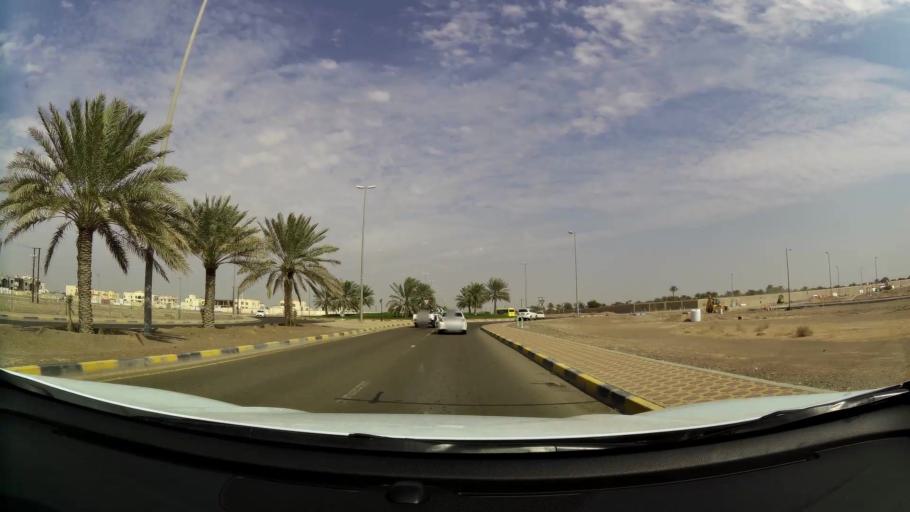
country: AE
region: Abu Dhabi
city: Al Ain
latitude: 24.0895
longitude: 55.8509
